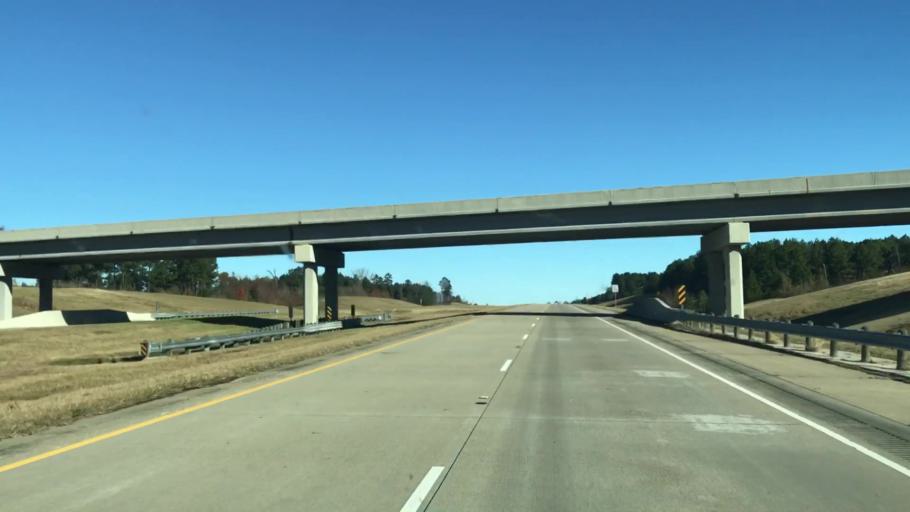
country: US
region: Louisiana
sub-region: Caddo Parish
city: Vivian
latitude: 33.0074
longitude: -93.9052
